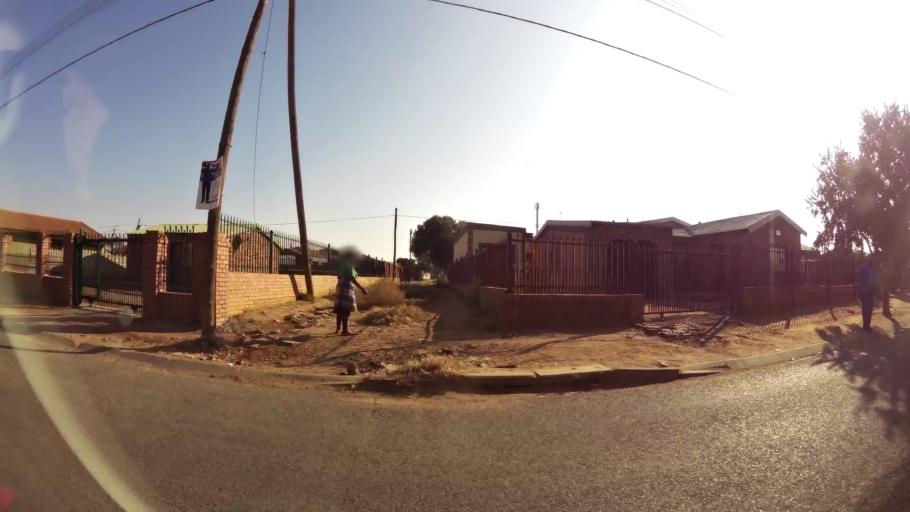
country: ZA
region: Orange Free State
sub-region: Mangaung Metropolitan Municipality
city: Bloemfontein
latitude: -29.2014
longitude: 26.2203
